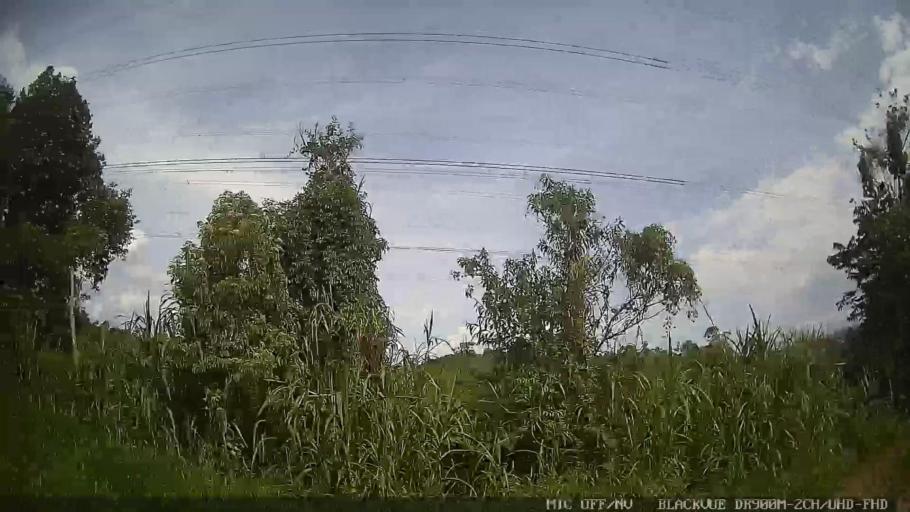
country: BR
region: Sao Paulo
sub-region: Mogi das Cruzes
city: Mogi das Cruzes
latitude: -23.6487
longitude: -46.2210
